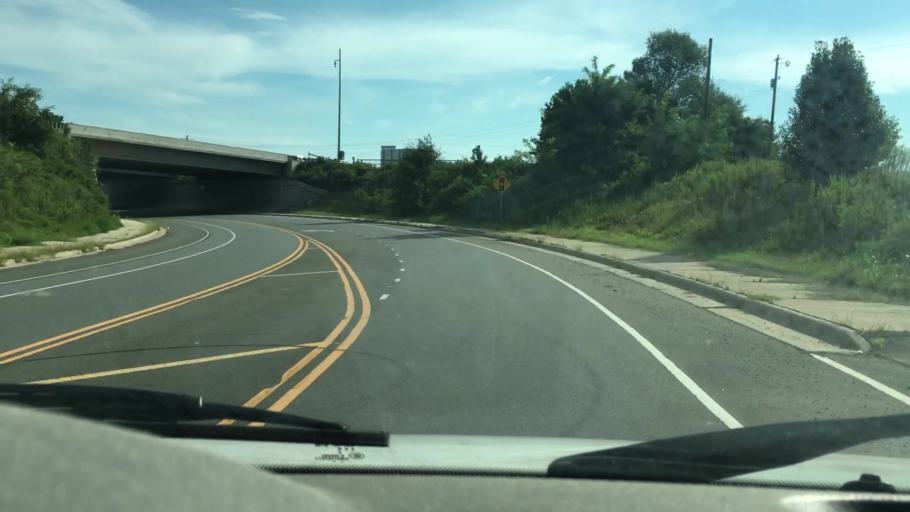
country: US
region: North Carolina
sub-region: Mecklenburg County
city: Huntersville
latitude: 35.3656
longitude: -80.8168
